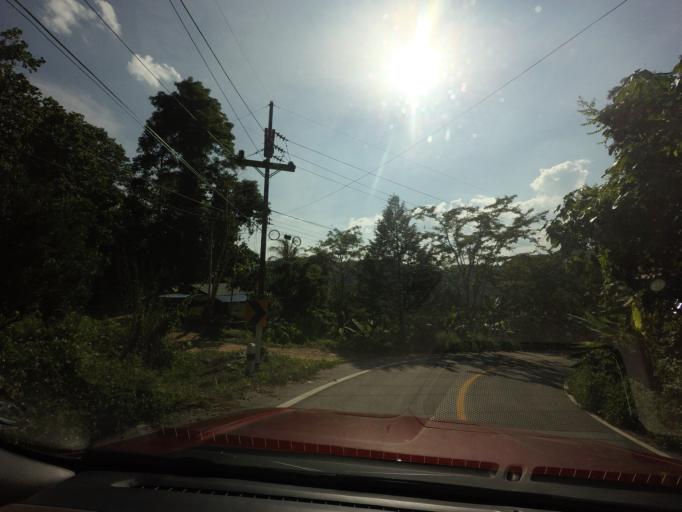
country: TH
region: Yala
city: Than To
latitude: 6.0719
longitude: 101.3432
